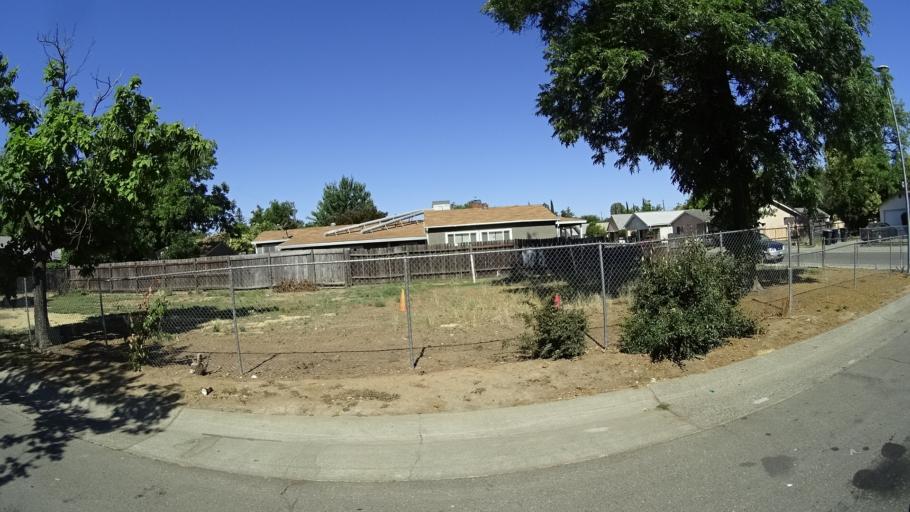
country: US
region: California
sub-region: Sacramento County
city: Parkway
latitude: 38.5410
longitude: -121.4531
